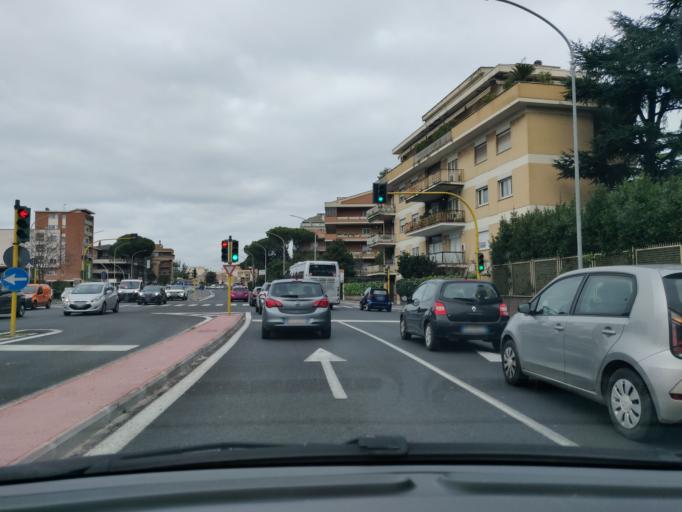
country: VA
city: Vatican City
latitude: 41.8906
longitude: 12.4128
